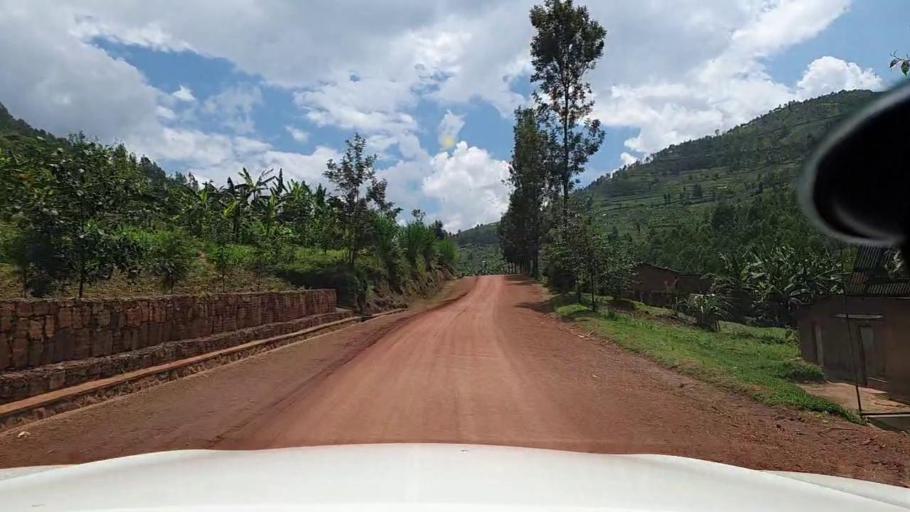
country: RW
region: Northern Province
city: Byumba
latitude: -1.7471
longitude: 29.8499
